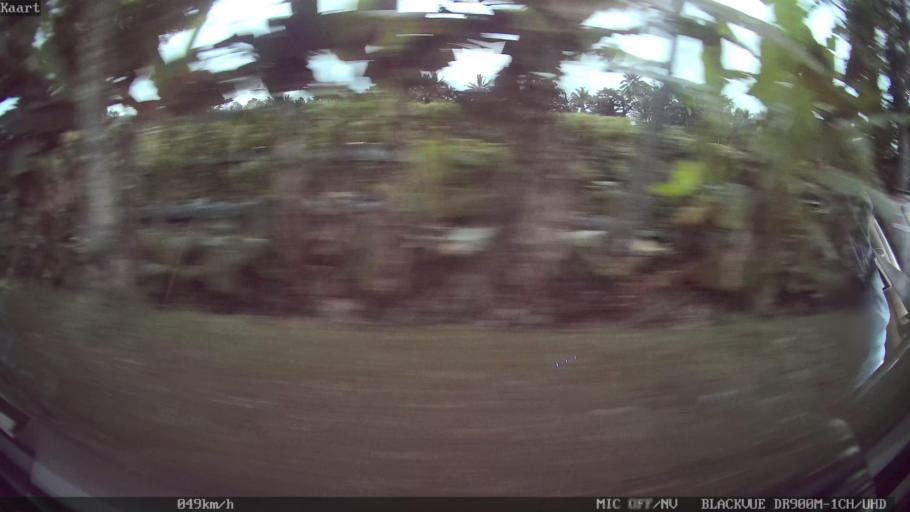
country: ID
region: Bali
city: Empalan
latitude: -8.4067
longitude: 115.1464
